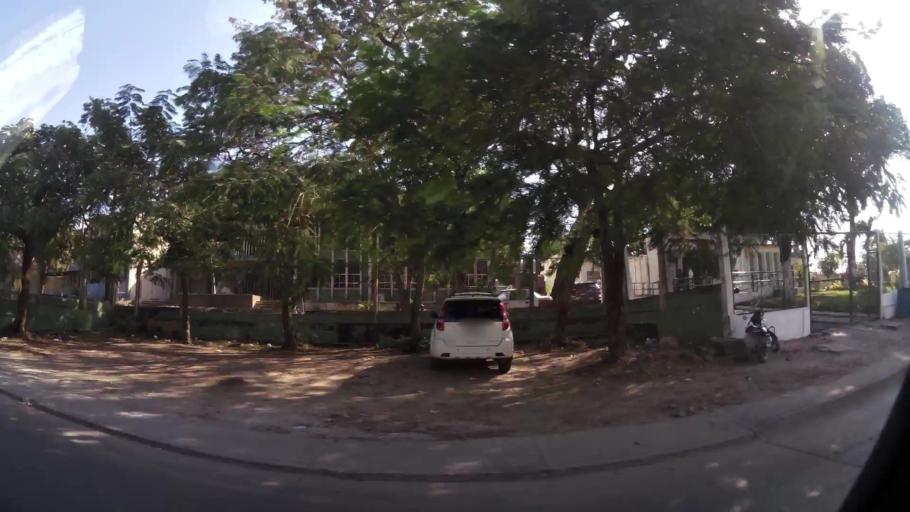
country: CO
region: Bolivar
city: Cartagena
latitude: 10.4060
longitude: -75.4936
